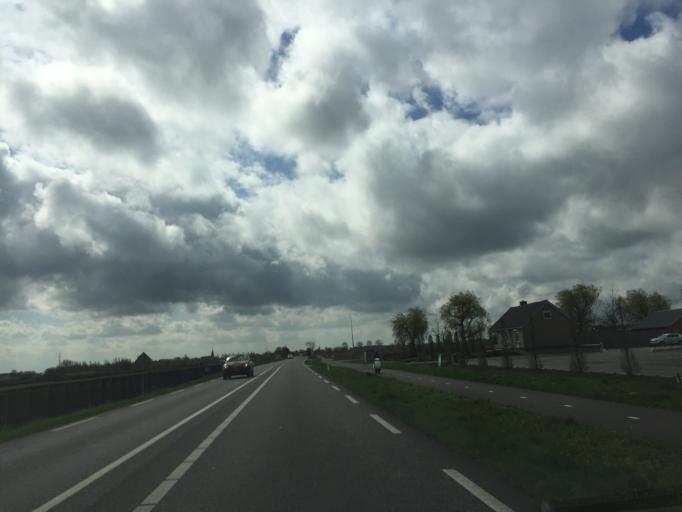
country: NL
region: South Holland
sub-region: Gemeente Rijnwoude
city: Benthuizen
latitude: 52.1105
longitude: 4.5880
